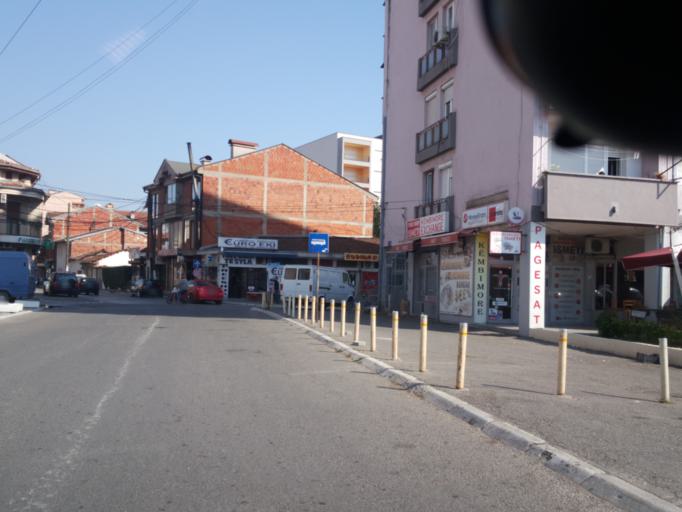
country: XK
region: Gjakova
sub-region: Komuna e Gjakoves
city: Gjakove
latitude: 42.3864
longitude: 20.4281
